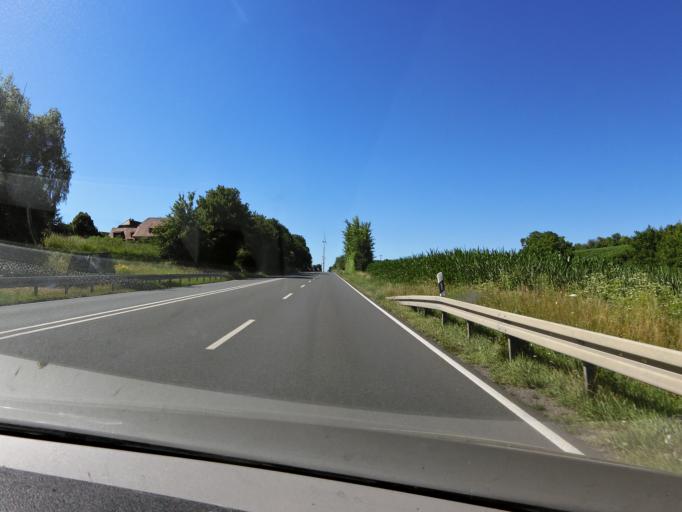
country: DE
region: Bavaria
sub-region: Regierungsbezirk Unterfranken
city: Buchbrunn
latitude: 49.7502
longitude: 10.1258
